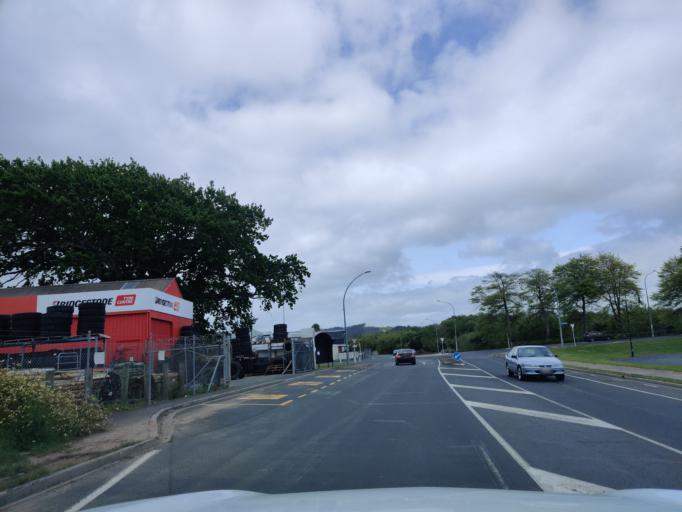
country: NZ
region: Waikato
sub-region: Waikato District
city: Ngaruawahia
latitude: -37.5659
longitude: 175.1580
